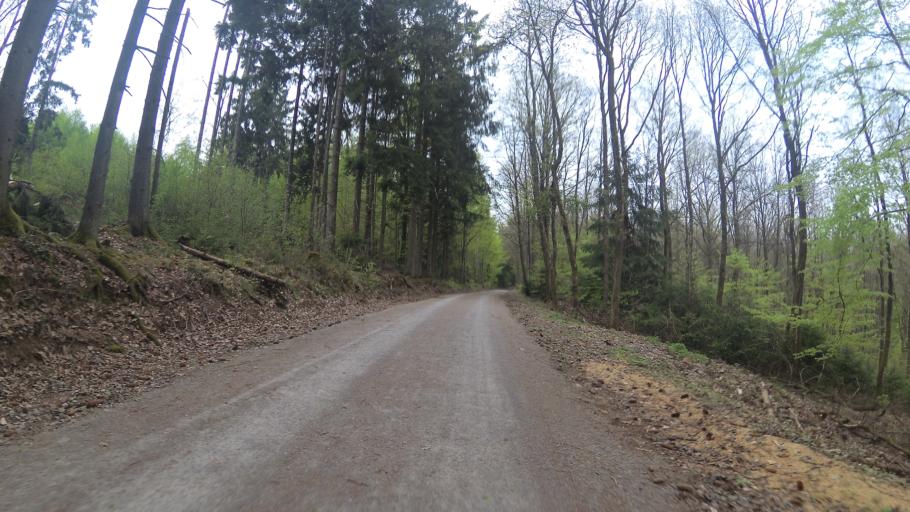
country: DE
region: Saarland
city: Mainzweiler
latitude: 49.4000
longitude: 7.1239
